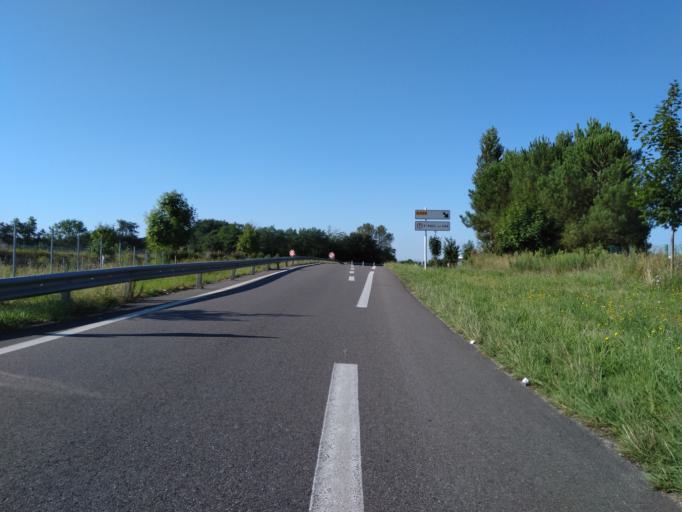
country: FR
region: Aquitaine
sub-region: Departement des Landes
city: Saint-Vincent-de-Paul
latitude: 43.7398
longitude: -1.0185
